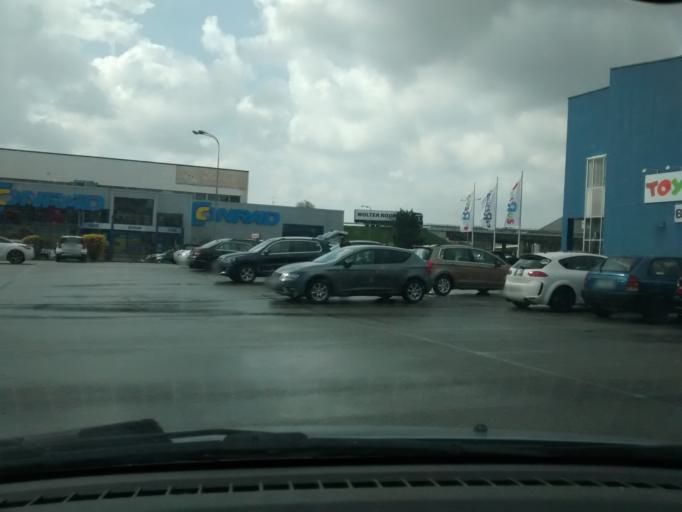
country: AT
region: Lower Austria
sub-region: Politischer Bezirk Modling
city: Vosendorf
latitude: 48.1151
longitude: 16.3180
